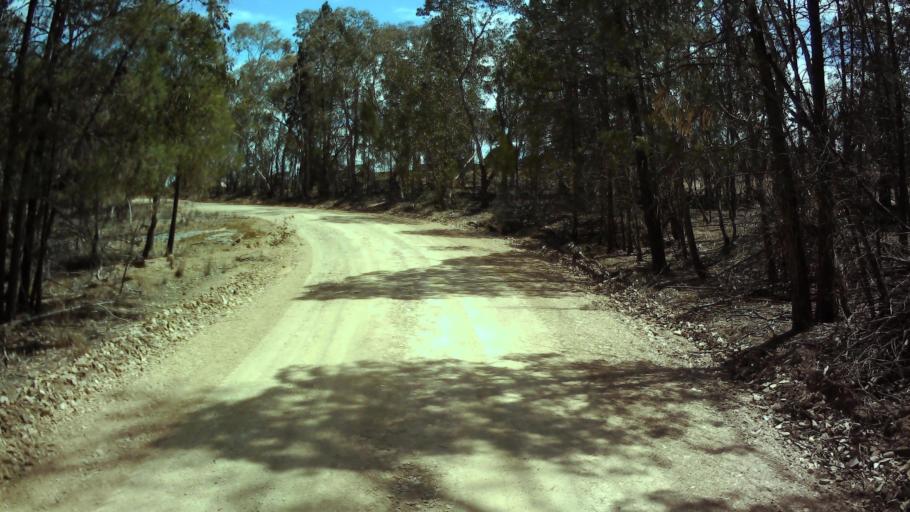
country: AU
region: New South Wales
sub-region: Weddin
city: Grenfell
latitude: -33.8091
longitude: 148.1585
